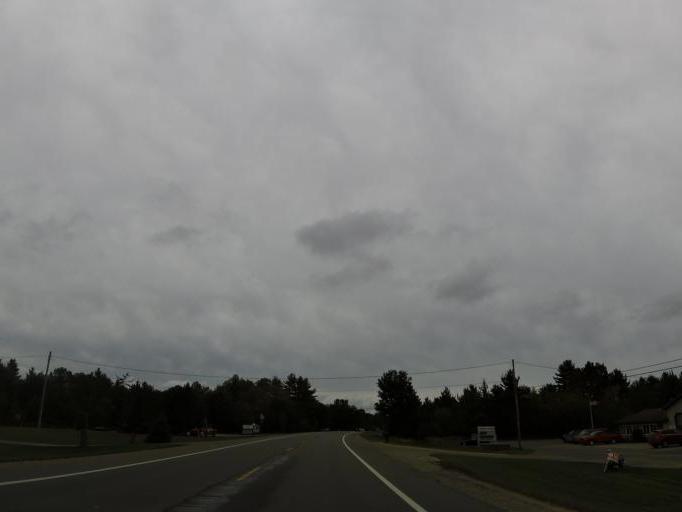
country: US
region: Michigan
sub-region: Roscommon County
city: Roscommon
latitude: 44.5098
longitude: -84.6122
